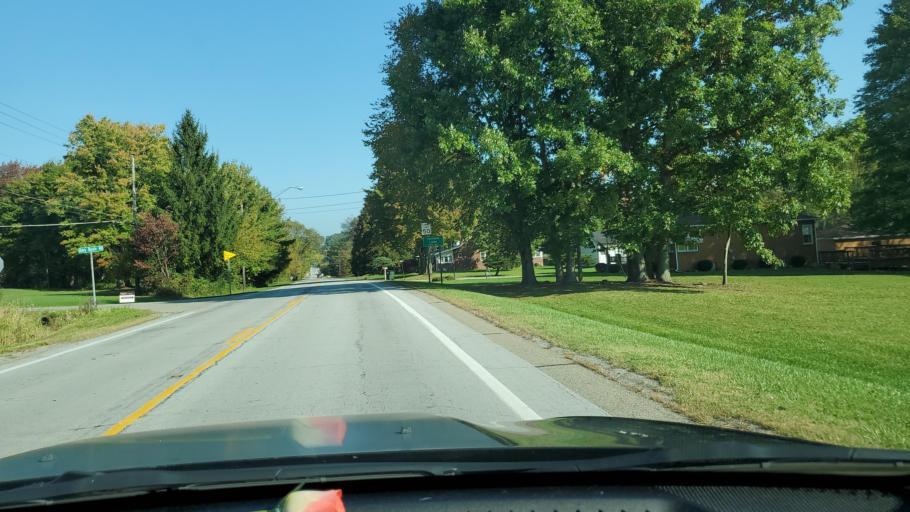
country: US
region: Ohio
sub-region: Trumbull County
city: Brookfield Center
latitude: 41.2638
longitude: -80.5681
